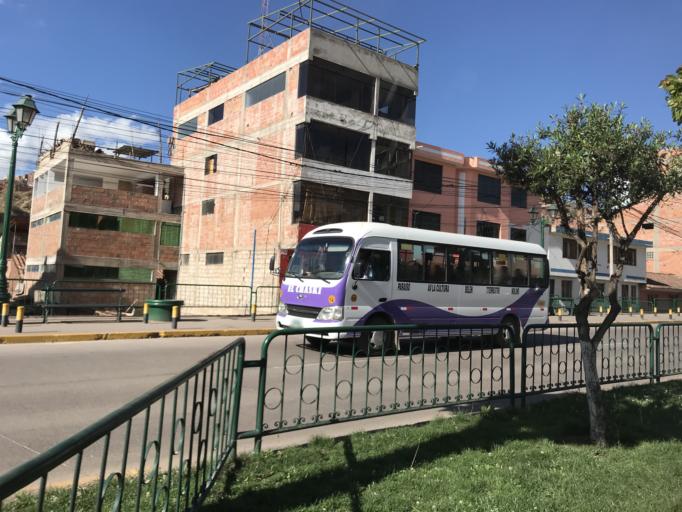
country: PE
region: Cusco
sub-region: Provincia de Cusco
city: Cusco
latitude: -13.5377
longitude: -71.9497
